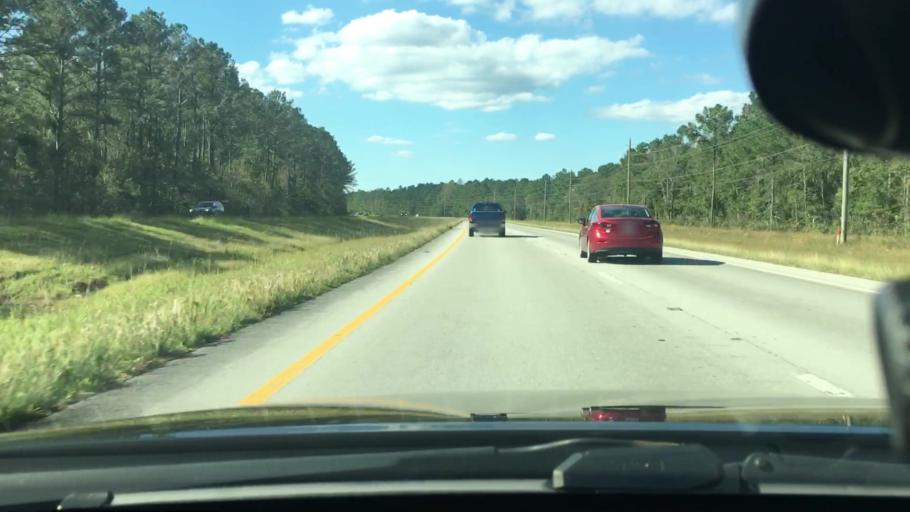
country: US
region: North Carolina
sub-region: Craven County
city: Neuse Forest
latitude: 34.9600
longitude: -76.9526
